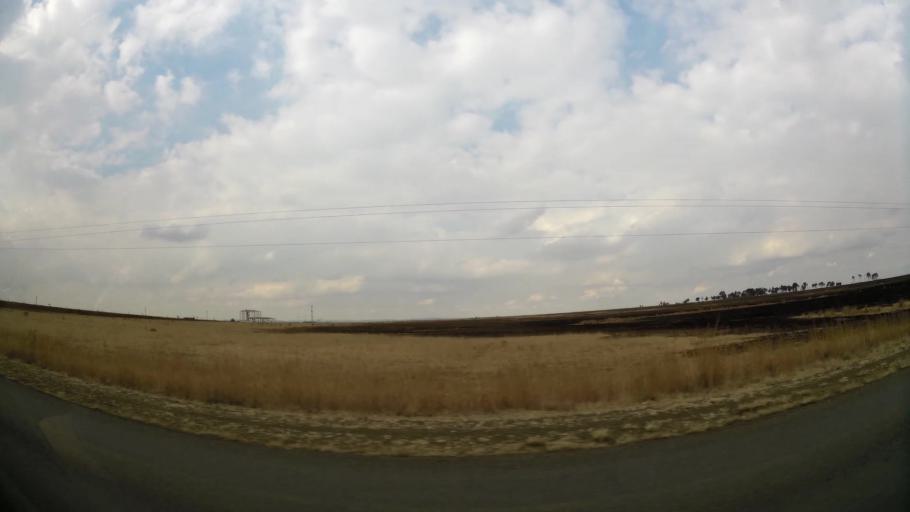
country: ZA
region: Orange Free State
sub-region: Fezile Dabi District Municipality
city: Sasolburg
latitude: -26.8691
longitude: 27.8875
